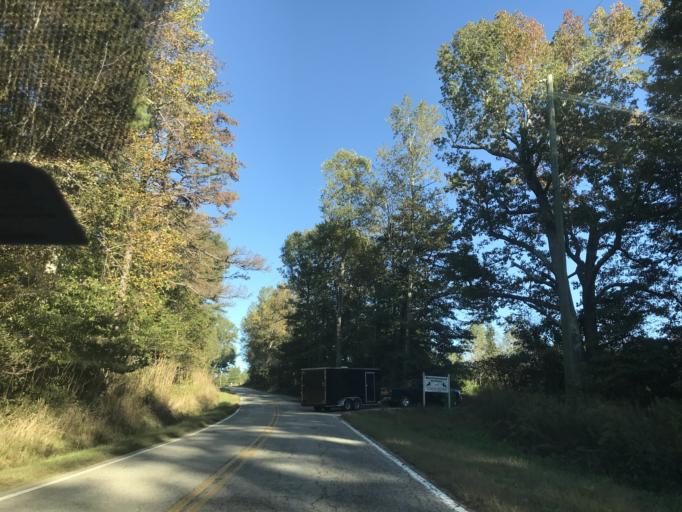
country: US
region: South Carolina
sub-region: Spartanburg County
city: Mayo
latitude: 35.1195
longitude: -81.8041
